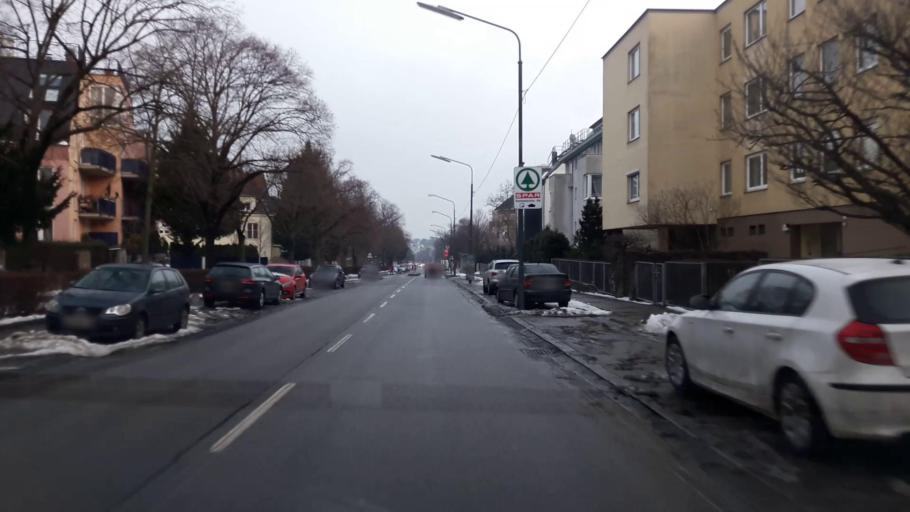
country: AT
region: Lower Austria
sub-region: Politischer Bezirk Wien-Umgebung
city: Klosterneuburg
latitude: 48.2471
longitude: 16.3135
